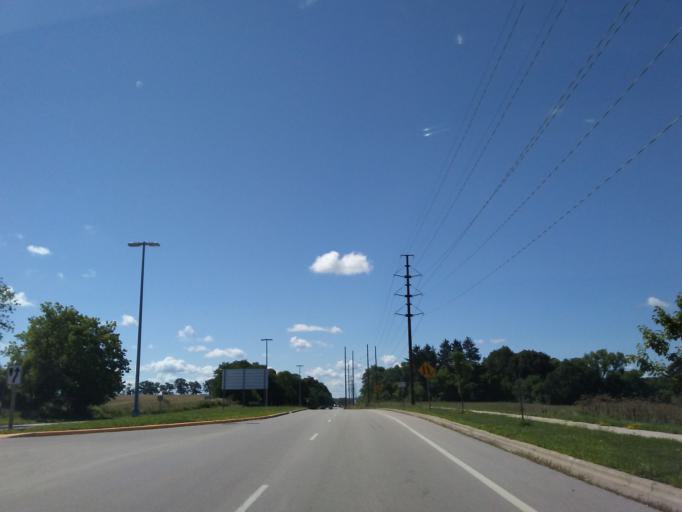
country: US
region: Wisconsin
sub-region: Dane County
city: Verona
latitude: 43.0443
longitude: -89.5329
